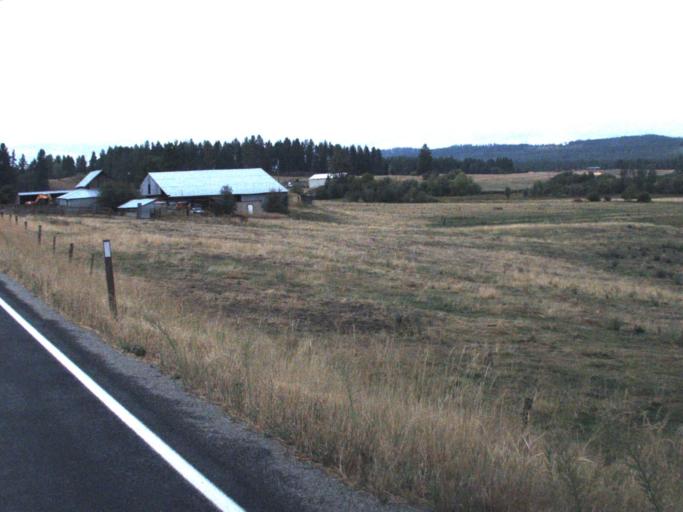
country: US
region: Washington
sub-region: Stevens County
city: Chewelah
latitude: 48.1275
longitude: -117.7441
